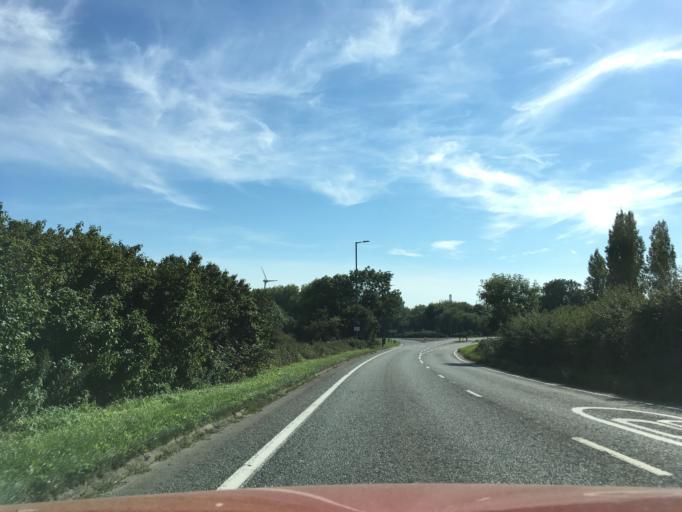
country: GB
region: England
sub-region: South Gloucestershire
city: Severn Beach
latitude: 51.5569
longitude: -2.6539
